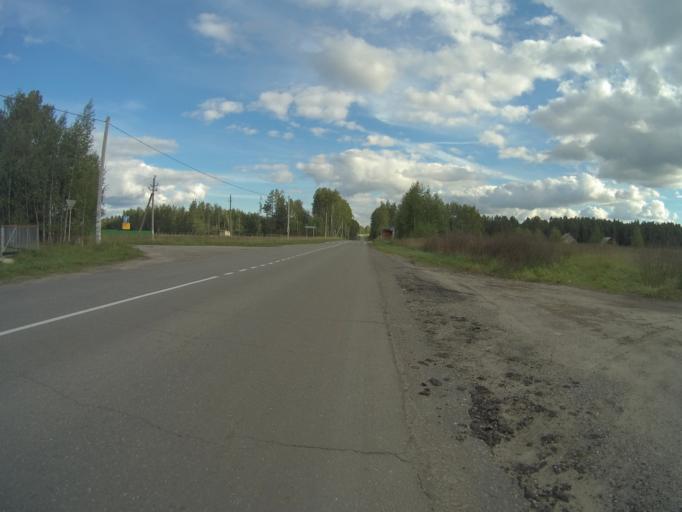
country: RU
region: Vladimir
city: Sudogda
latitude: 56.0588
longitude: 40.8163
